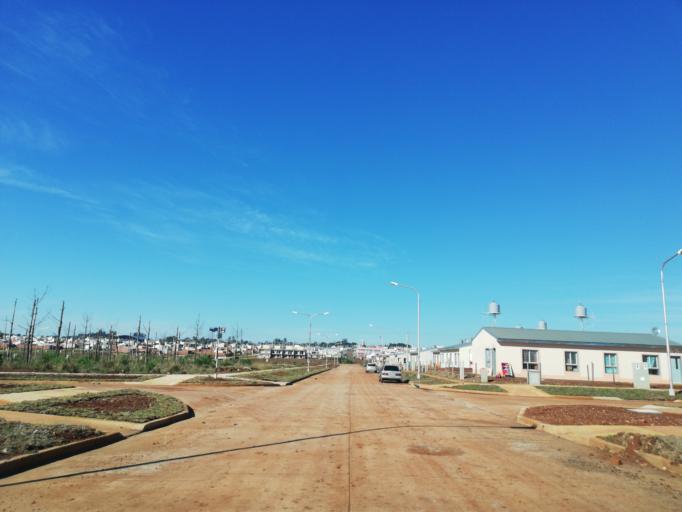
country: AR
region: Misiones
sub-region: Departamento de Capital
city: Posadas
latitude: -27.4075
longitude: -55.9915
